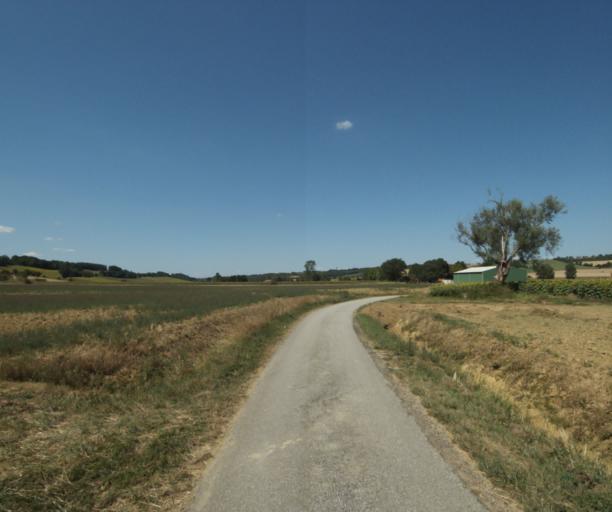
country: FR
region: Midi-Pyrenees
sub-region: Departement de la Haute-Garonne
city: Saint-Felix-Lauragais
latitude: 43.4826
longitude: 1.8761
